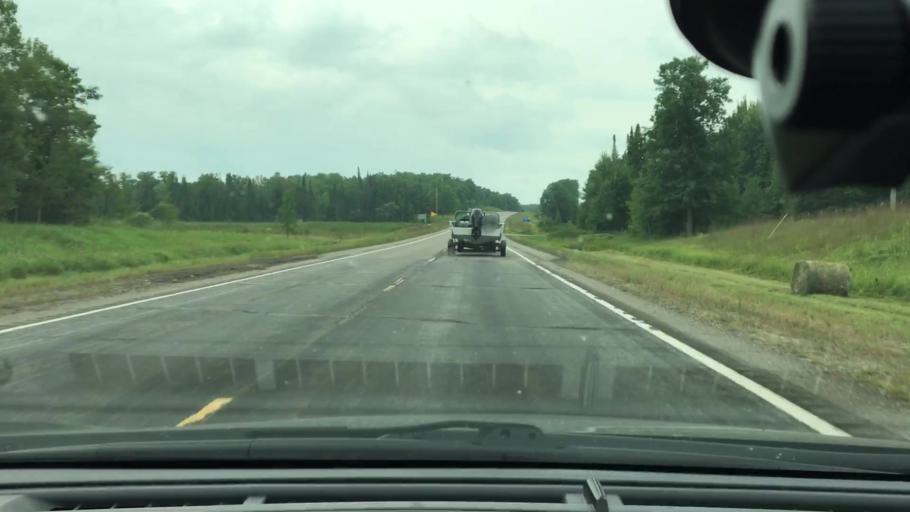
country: US
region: Minnesota
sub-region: Crow Wing County
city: Crosby
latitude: 46.6247
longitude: -93.9464
